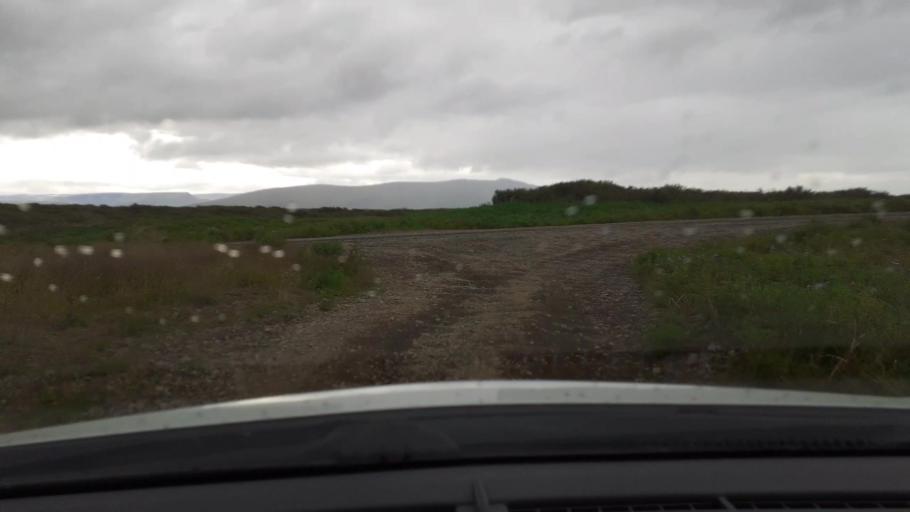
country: IS
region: West
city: Borgarnes
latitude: 64.4553
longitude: -21.9515
